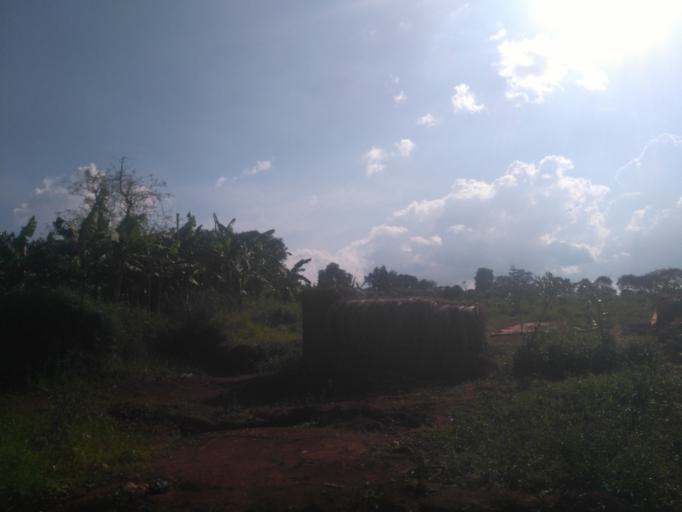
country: UG
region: Central Region
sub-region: Wakiso District
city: Wakiso
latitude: 0.3077
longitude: 32.4451
